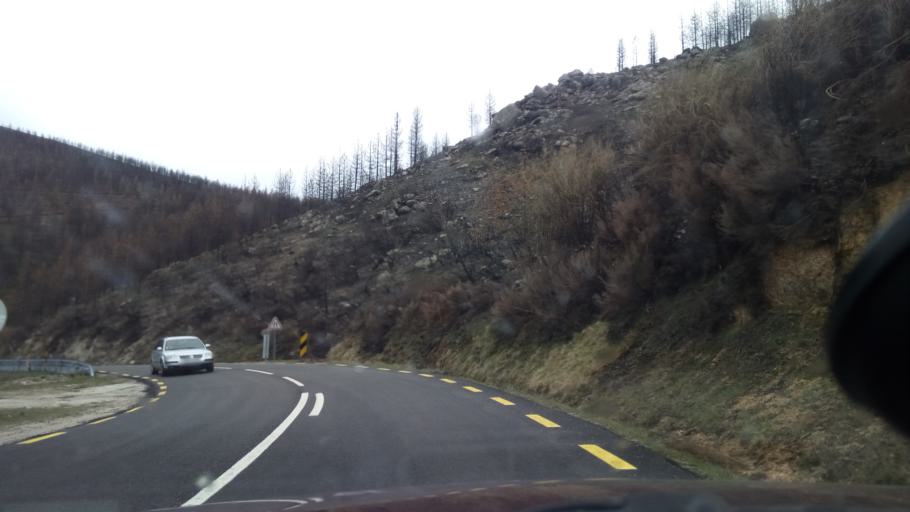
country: PT
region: Guarda
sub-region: Manteigas
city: Manteigas
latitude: 40.4399
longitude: -7.5977
